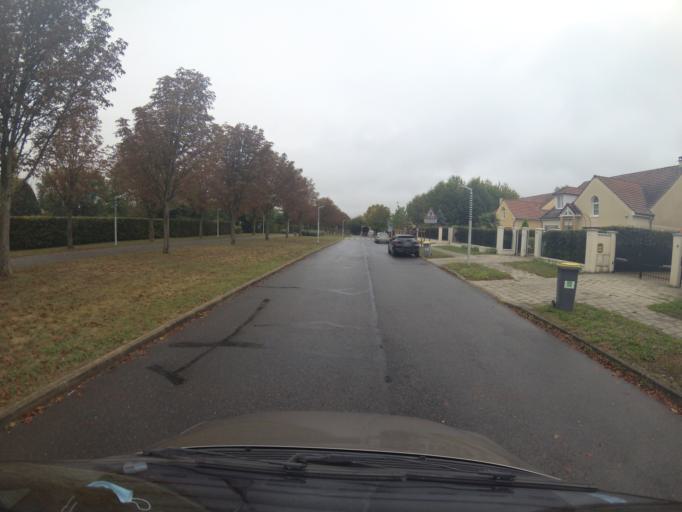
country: FR
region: Ile-de-France
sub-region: Departement de Seine-et-Marne
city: Conches-sur-Gondoire
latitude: 48.8473
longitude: 2.7262
